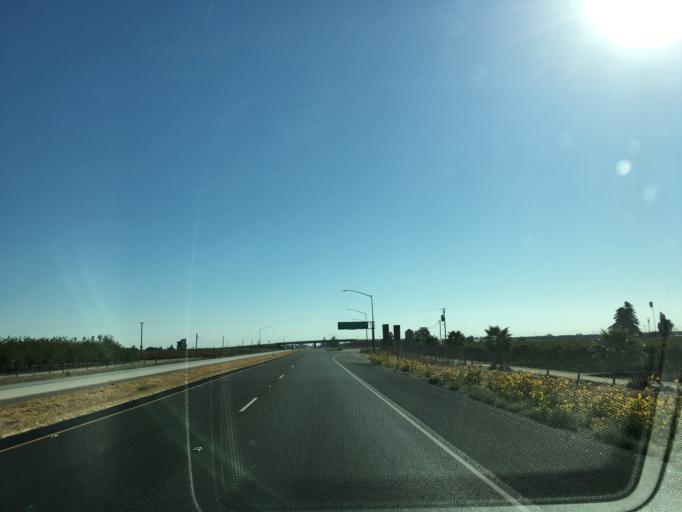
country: US
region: California
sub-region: Madera County
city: Chowchilla
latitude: 37.0834
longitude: -120.3040
